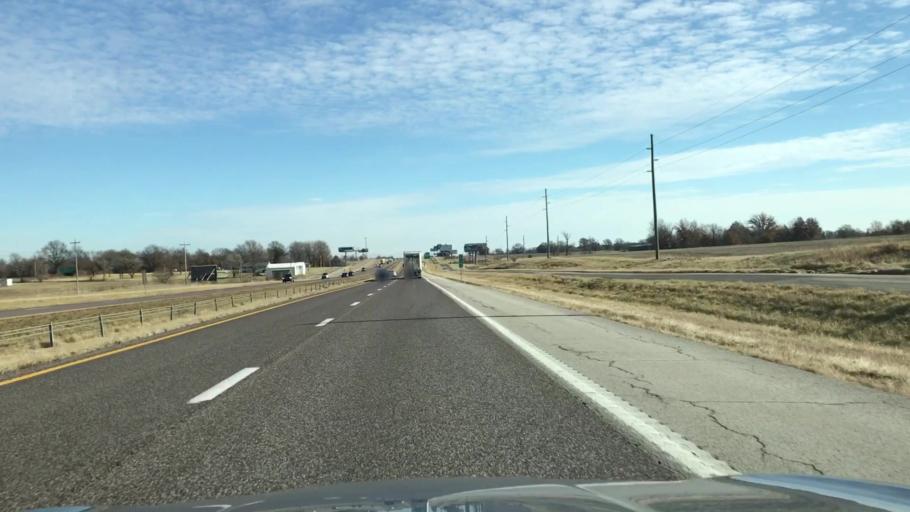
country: US
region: Missouri
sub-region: Callaway County
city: Fulton
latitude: 38.9520
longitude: -92.0375
